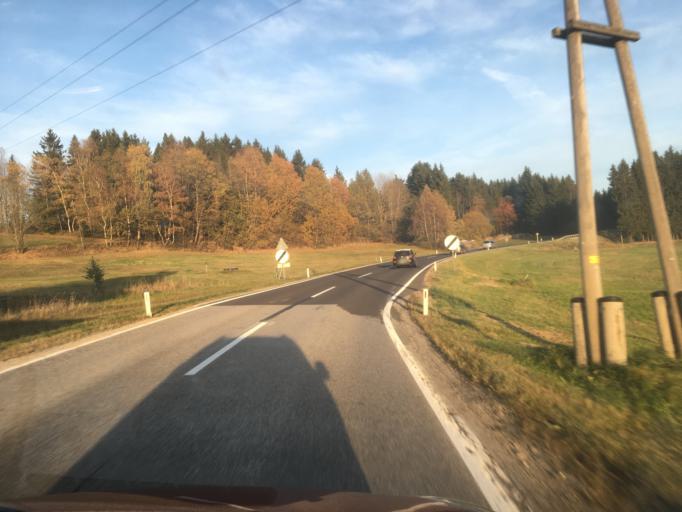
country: AT
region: Upper Austria
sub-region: Politischer Bezirk Freistadt
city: Freistadt
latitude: 48.5279
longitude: 14.5758
